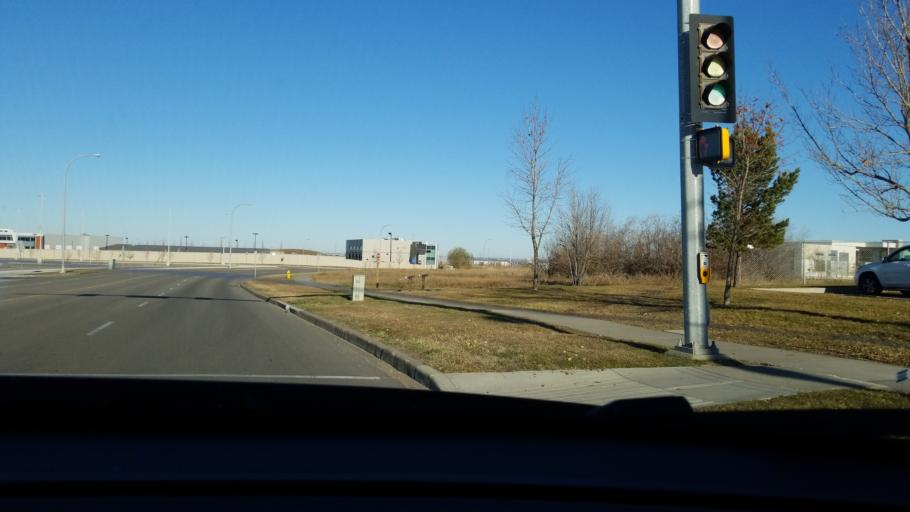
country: CA
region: Alberta
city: Sherwood Park
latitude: 53.5430
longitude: -113.3036
